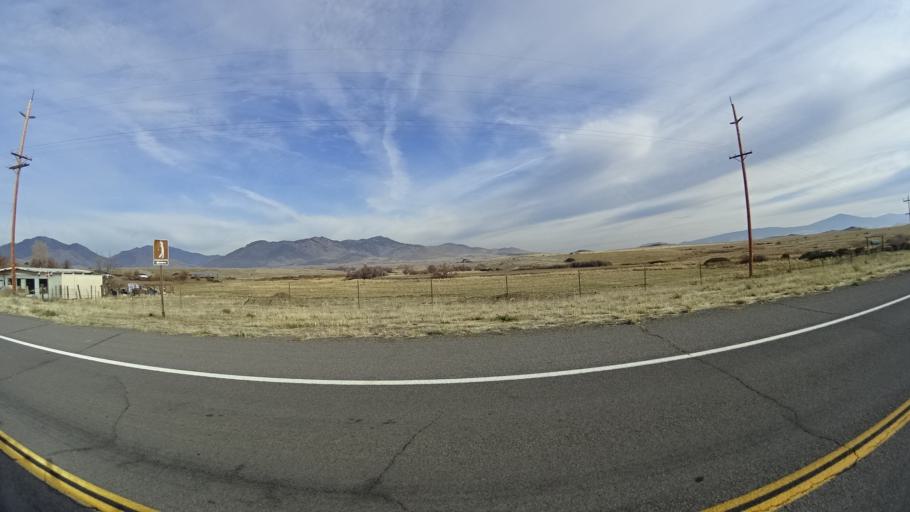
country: US
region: California
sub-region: Siskiyou County
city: Montague
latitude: 41.7286
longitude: -122.5632
